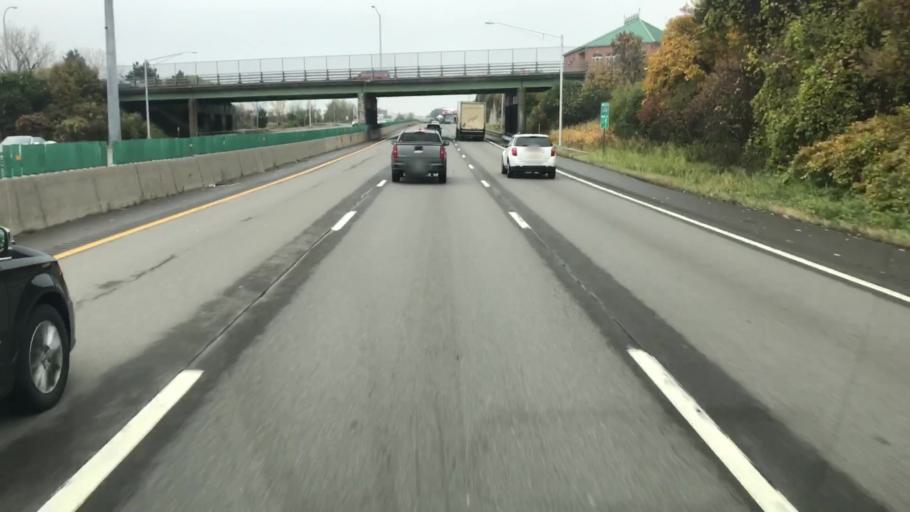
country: US
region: New York
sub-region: Onondaga County
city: East Syracuse
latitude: 43.0580
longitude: -76.1030
